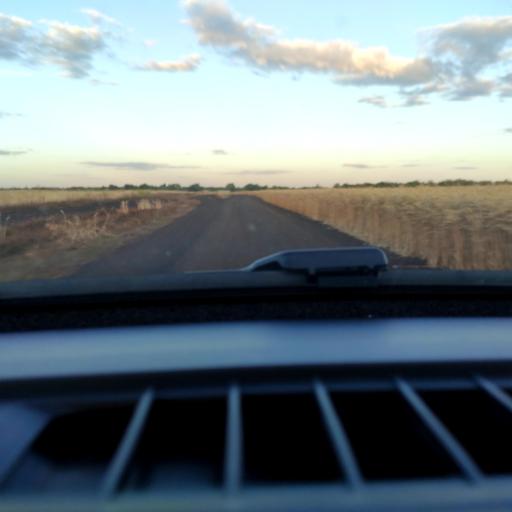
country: RU
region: Voronezj
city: Verkhnyaya Khava
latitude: 51.6101
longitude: 39.8267
